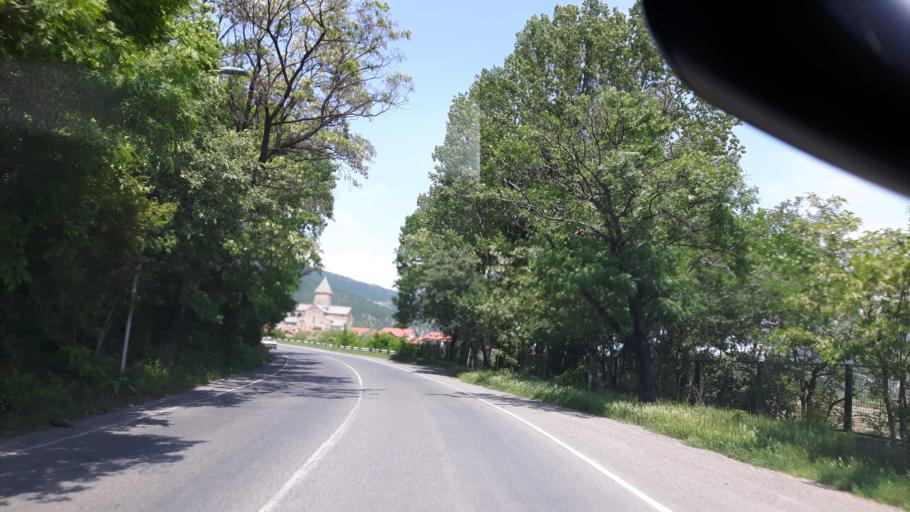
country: GE
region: Mtskheta-Mtianeti
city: Mtskheta
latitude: 41.8373
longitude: 44.7233
